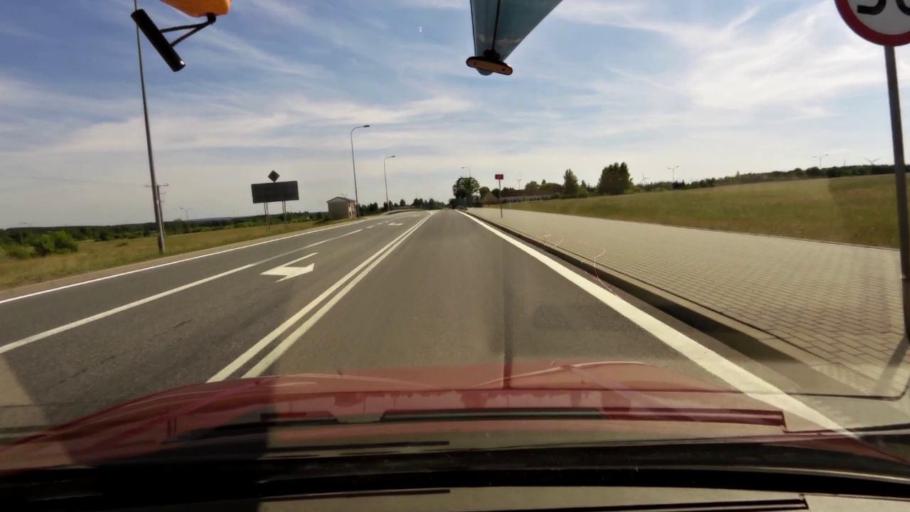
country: PL
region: Pomeranian Voivodeship
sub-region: Powiat slupski
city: Kobylnica
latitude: 54.4260
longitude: 17.0071
